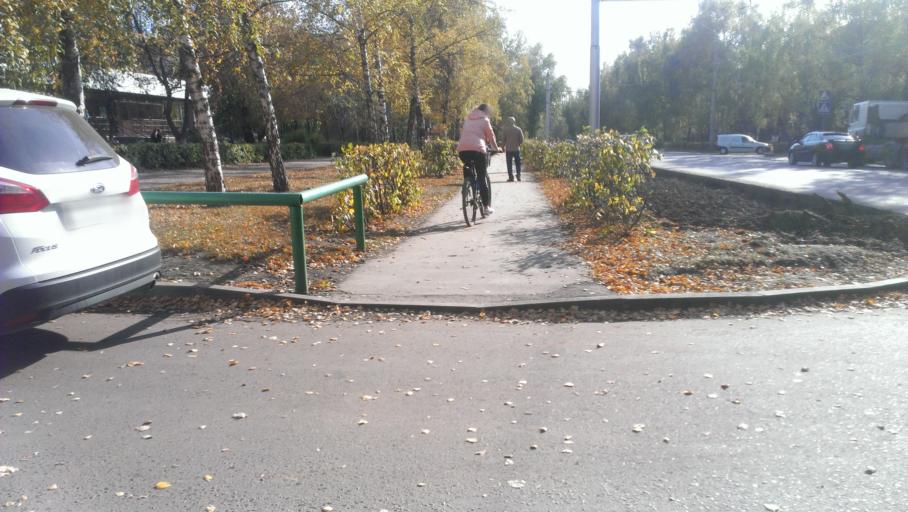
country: RU
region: Altai Krai
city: Novosilikatnyy
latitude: 53.3533
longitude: 83.6843
